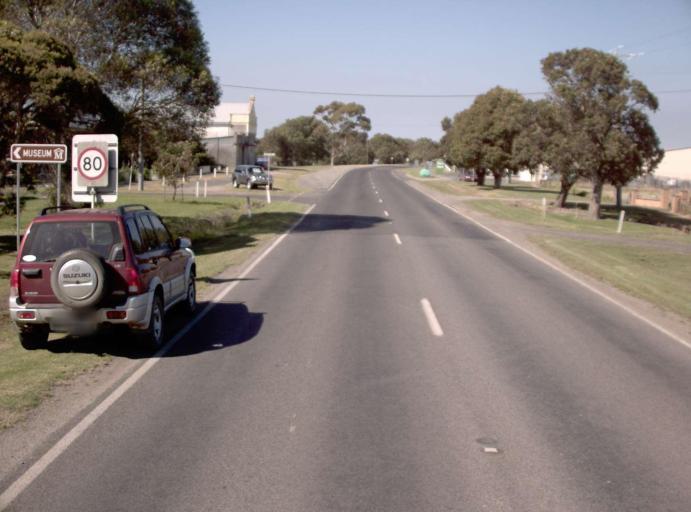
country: AU
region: Victoria
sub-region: Latrobe
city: Traralgon
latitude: -38.5537
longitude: 146.6799
